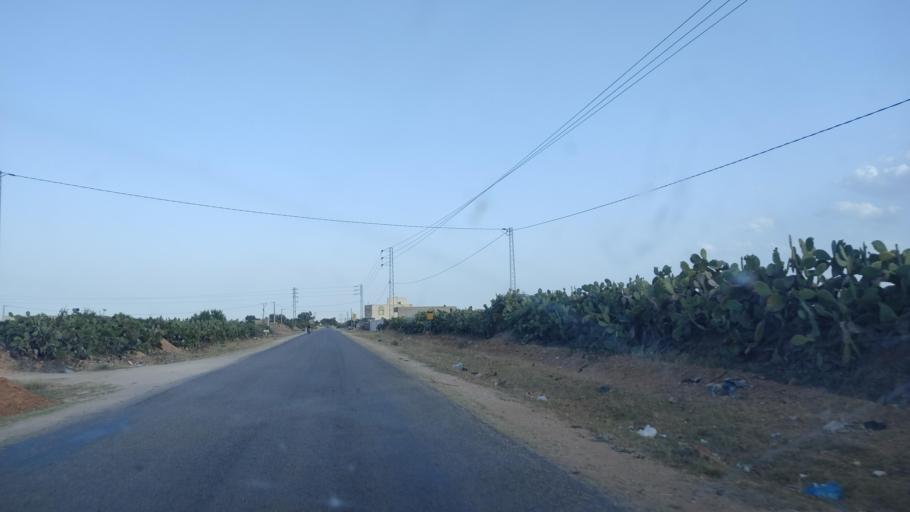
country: TN
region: Safaqis
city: Sfax
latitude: 34.8129
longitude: 10.6594
